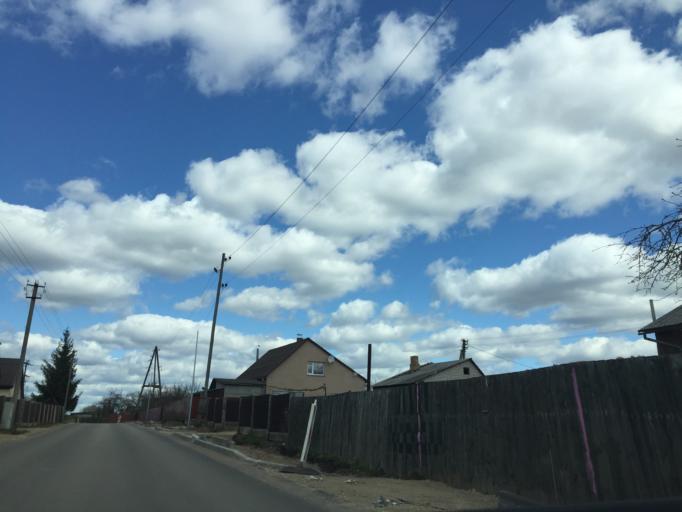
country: LV
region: Rezekne
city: Rezekne
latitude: 56.4885
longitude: 27.3242
